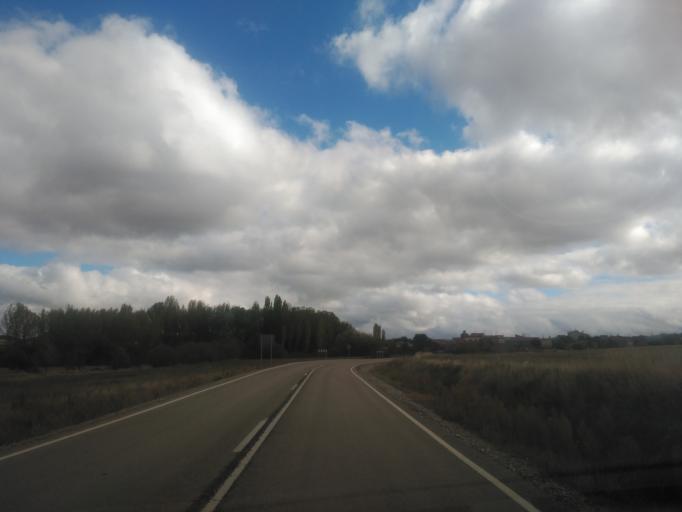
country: ES
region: Castille and Leon
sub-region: Provincia de Soria
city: Espeja de San Marcelino
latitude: 41.7581
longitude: -3.2397
